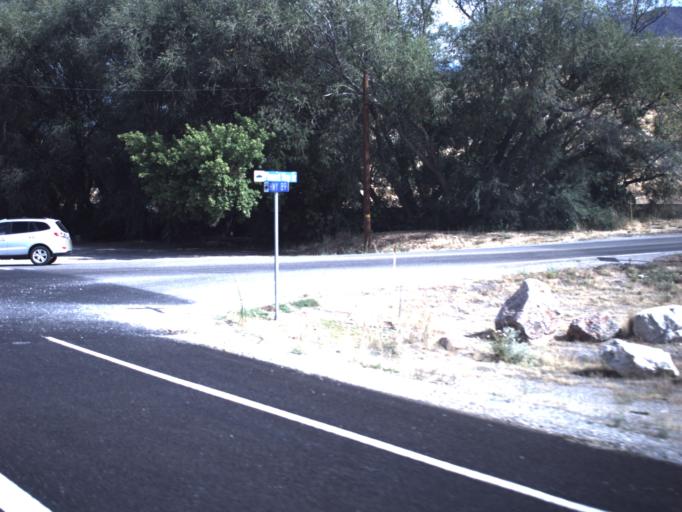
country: US
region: Utah
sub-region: Box Elder County
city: South Willard
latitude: 41.3339
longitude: -112.0261
